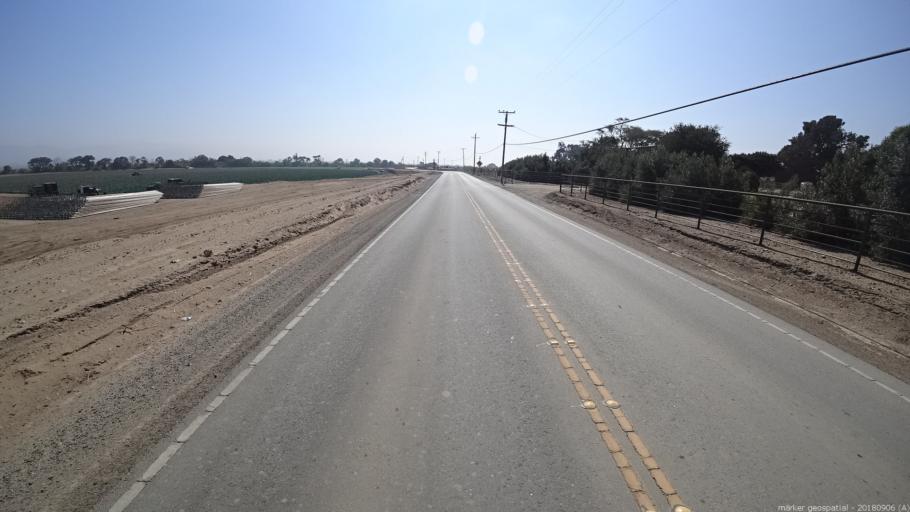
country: US
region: California
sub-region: Monterey County
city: Chualar
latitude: 36.5619
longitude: -121.5577
